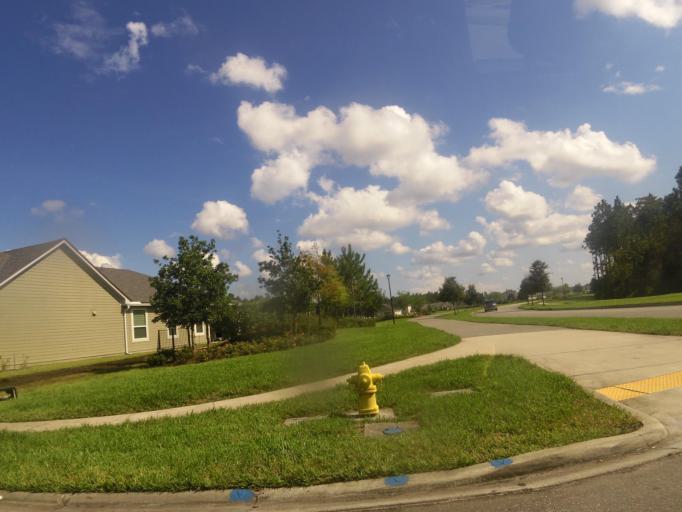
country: US
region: Florida
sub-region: Saint Johns County
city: Palm Valley
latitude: 30.0790
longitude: -81.4689
